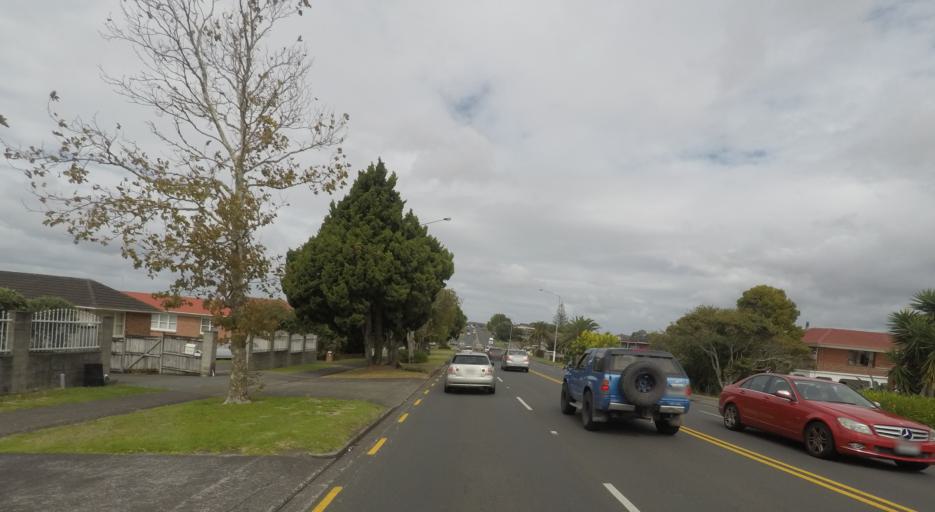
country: NZ
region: Auckland
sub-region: Auckland
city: Rosebank
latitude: -36.8884
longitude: 174.6446
